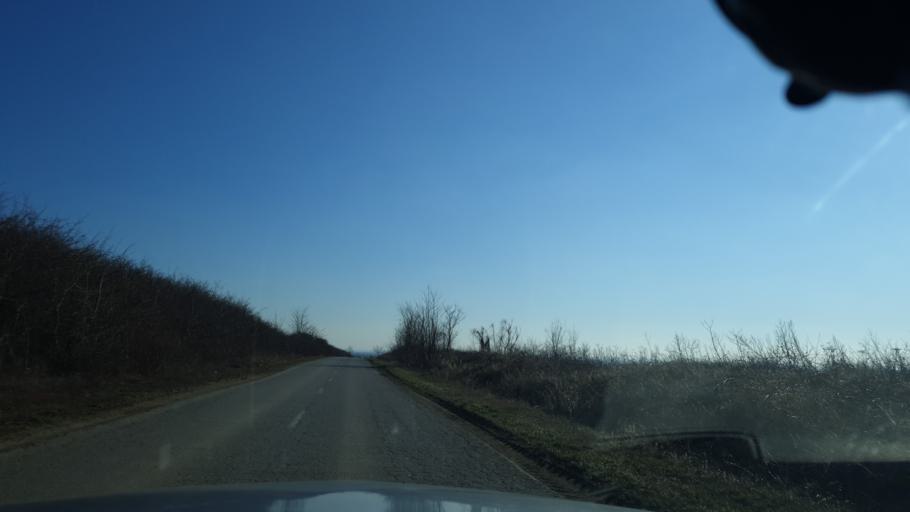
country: RS
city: Vrdnik
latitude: 45.0948
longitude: 19.8053
